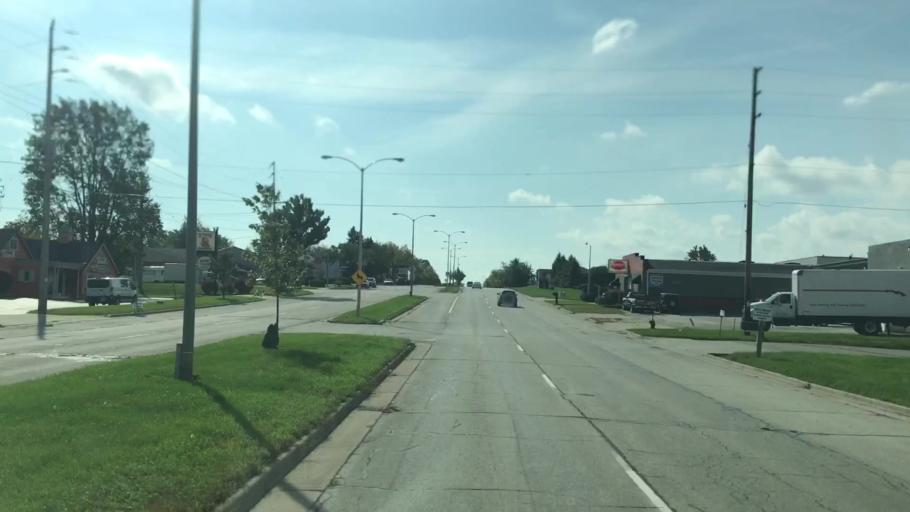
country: US
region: Wisconsin
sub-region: Waukesha County
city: Menomonee Falls
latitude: 43.1759
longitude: -88.0443
